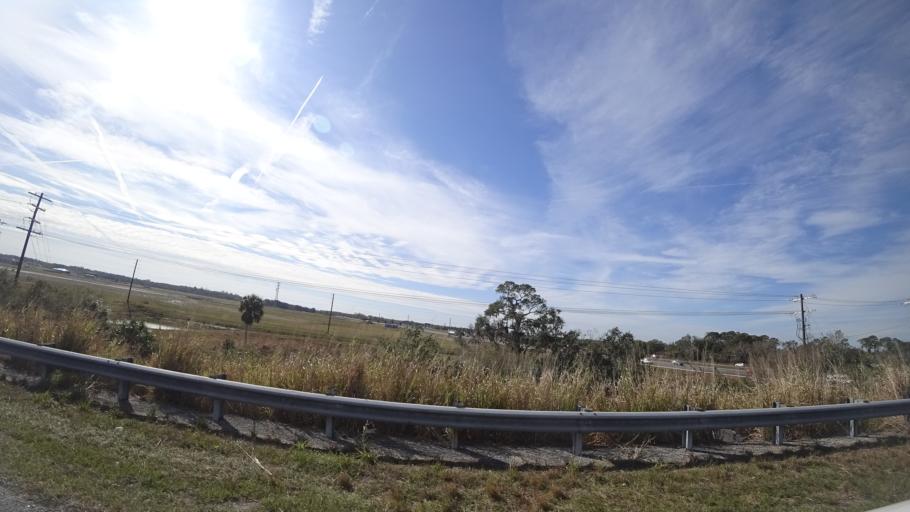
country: US
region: Florida
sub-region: Manatee County
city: Ellenton
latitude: 27.5739
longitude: -82.5132
